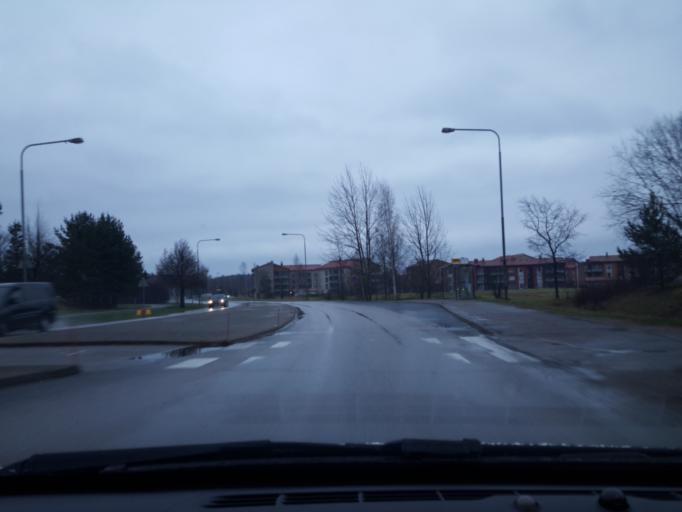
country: FI
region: Uusimaa
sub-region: Helsinki
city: Vantaa
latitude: 60.3117
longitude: 25.0391
